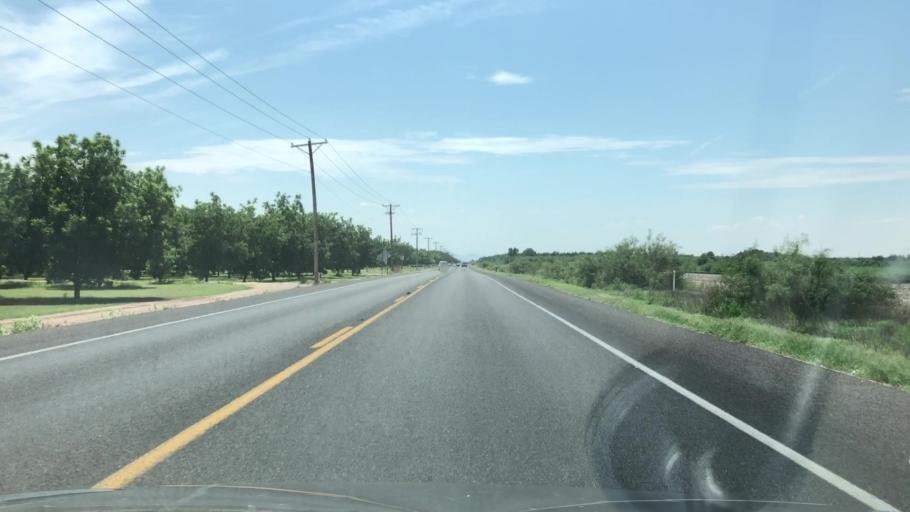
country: US
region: New Mexico
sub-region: Dona Ana County
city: University Park
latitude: 32.2347
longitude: -106.7409
